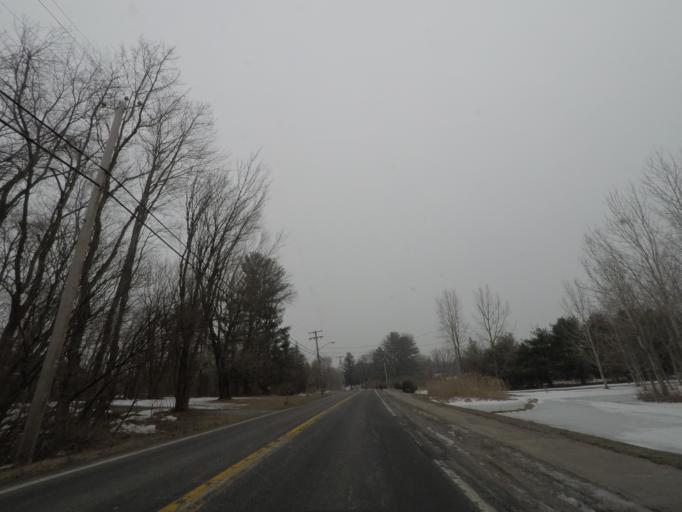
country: US
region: New York
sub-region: Rensselaer County
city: Castleton-on-Hudson
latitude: 42.5403
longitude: -73.8024
